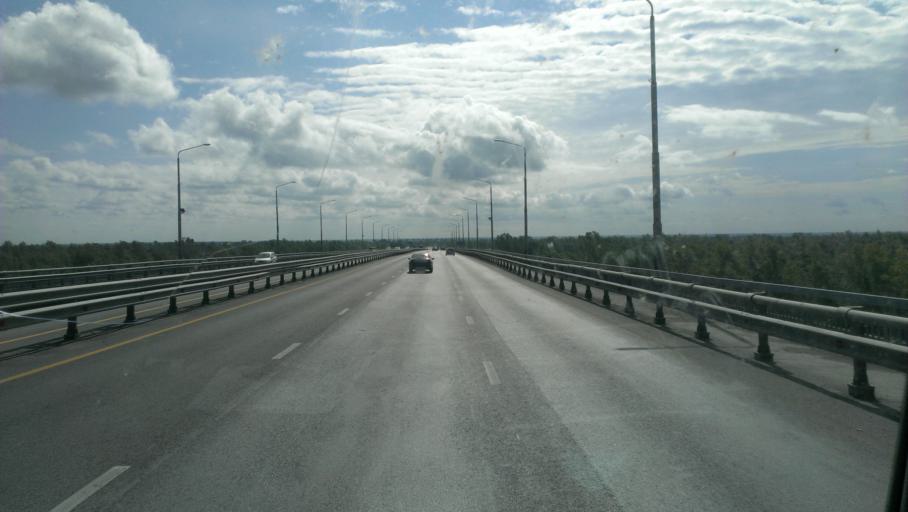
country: RU
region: Altai Krai
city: Zaton
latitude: 53.3228
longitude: 83.8053
